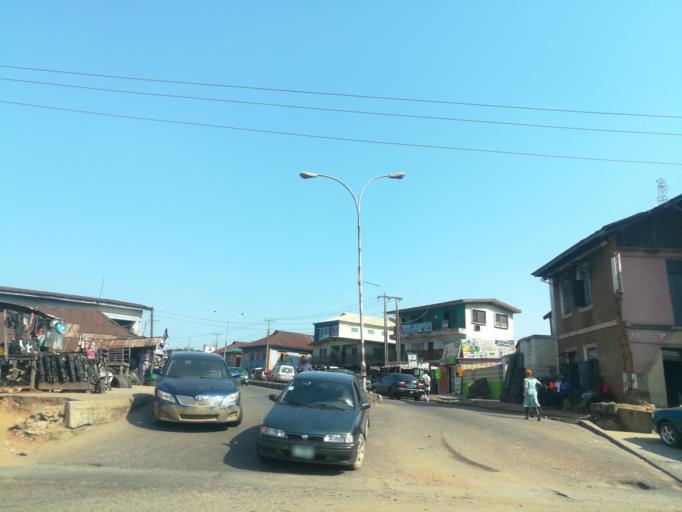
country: NG
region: Ogun
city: Abeokuta
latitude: 7.1475
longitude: 3.3424
